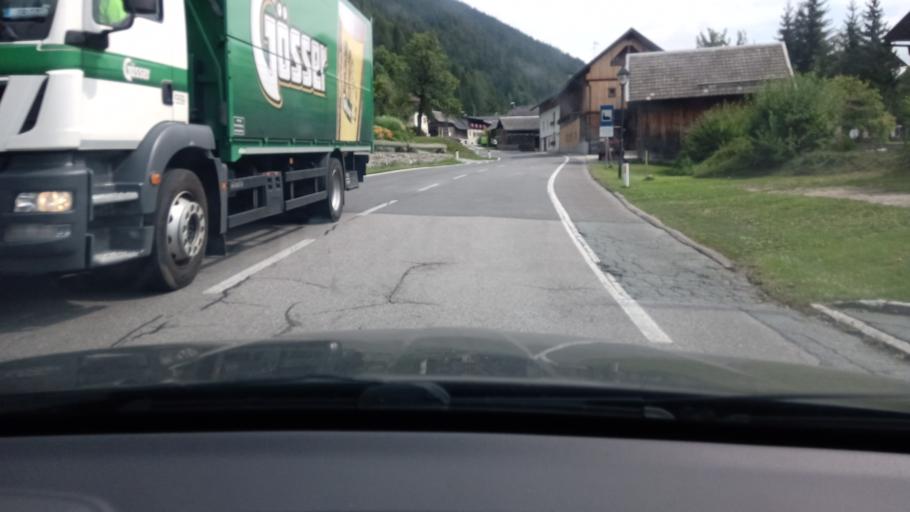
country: AT
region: Carinthia
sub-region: Politischer Bezirk Spittal an der Drau
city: Steinfeld
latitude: 46.7232
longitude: 13.2703
